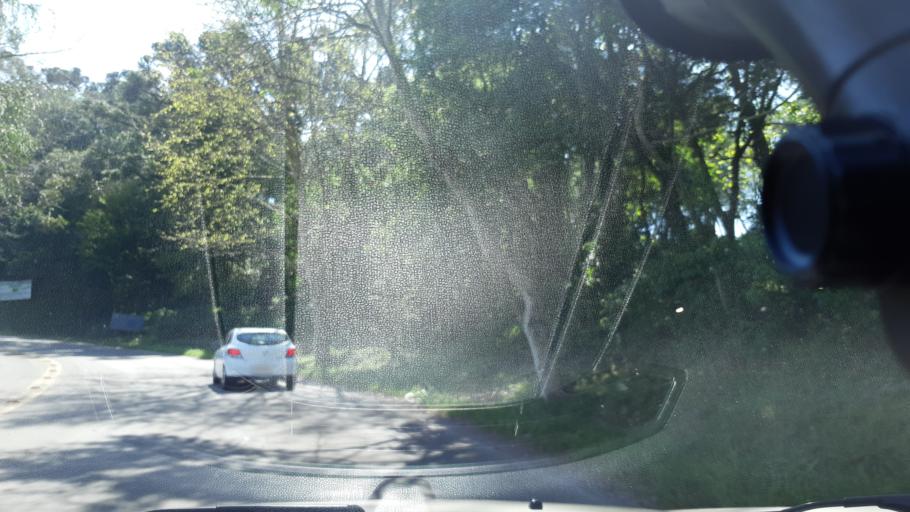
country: BR
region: Rio Grande do Sul
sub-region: Nova Petropolis
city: Nova Petropolis
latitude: -29.3892
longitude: -51.1258
